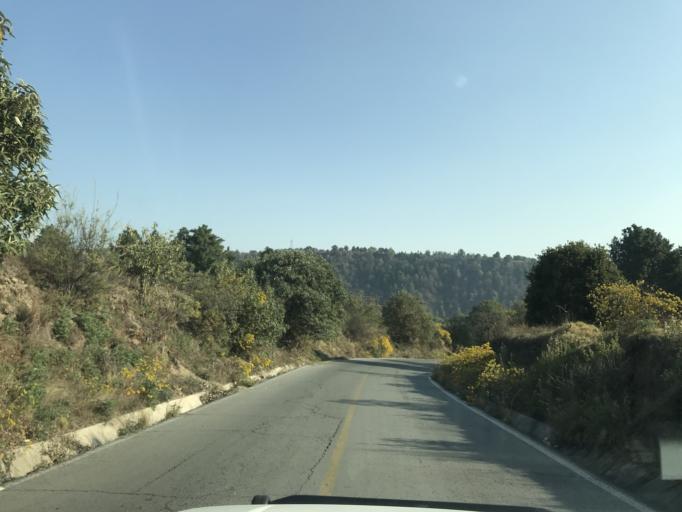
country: MX
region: Puebla
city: San Nicolas de los Ranchos
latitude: 19.0855
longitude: -98.5316
